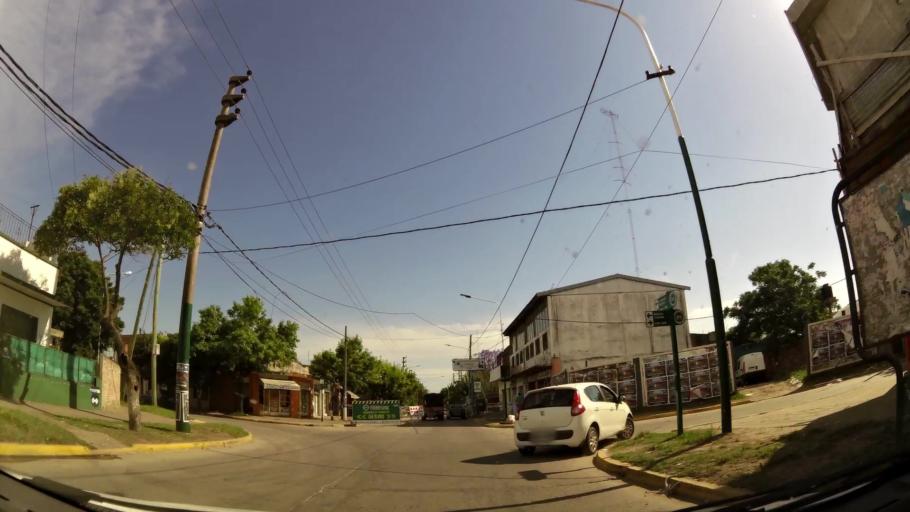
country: AR
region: Buenos Aires
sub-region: Partido de Merlo
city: Merlo
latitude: -34.6498
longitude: -58.7207
